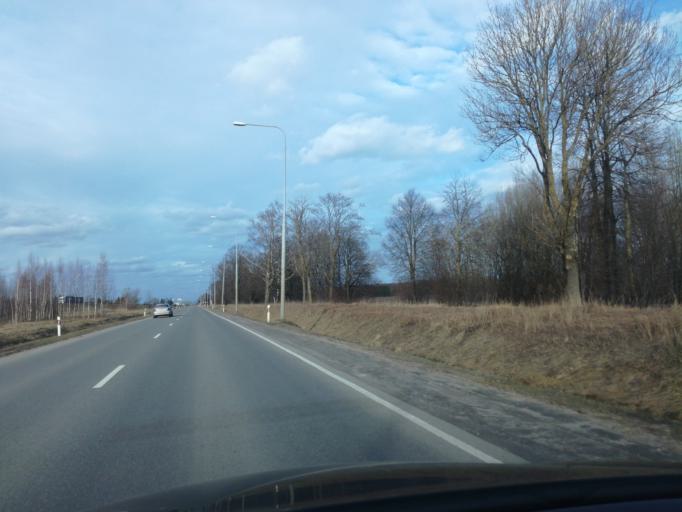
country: LT
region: Marijampoles apskritis
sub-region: Marijampole Municipality
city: Marijampole
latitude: 54.5823
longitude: 23.3781
